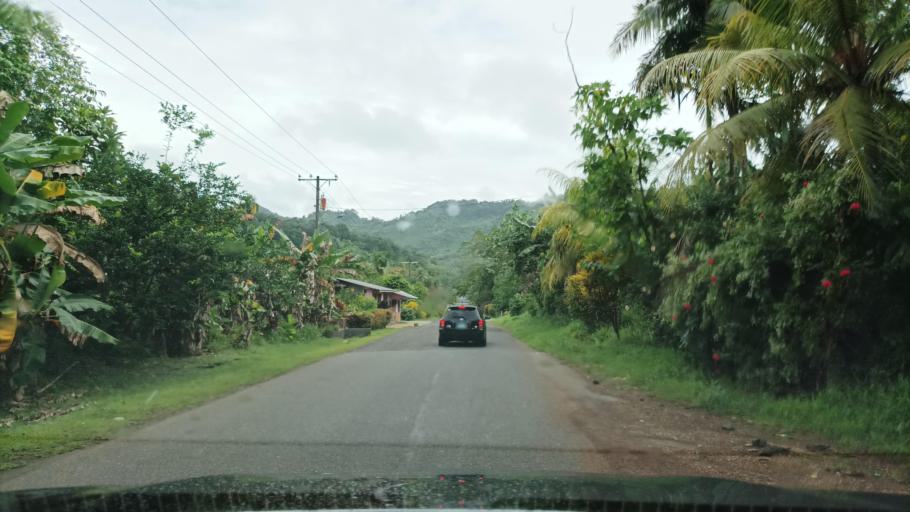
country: FM
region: Pohnpei
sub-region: Madolenihm Municipality
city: Madolenihm Municipality Government
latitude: 6.9212
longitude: 158.2878
